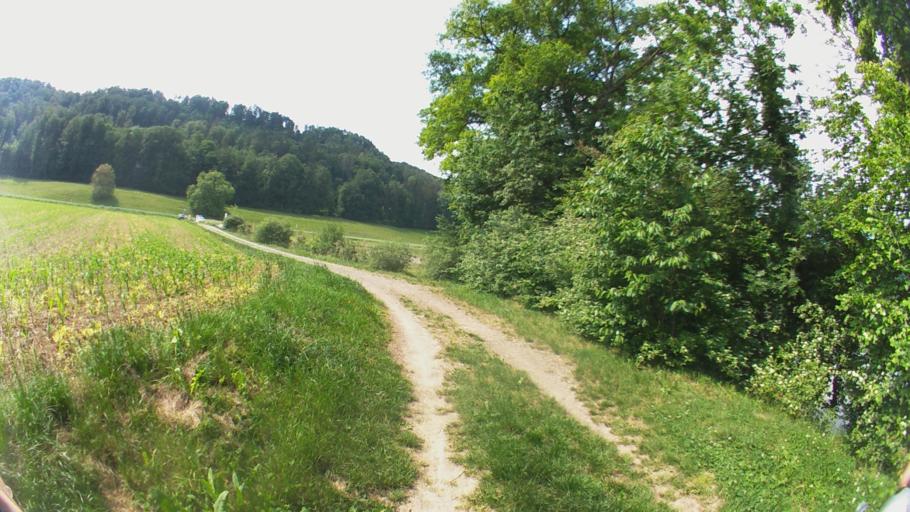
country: CH
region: Zurich
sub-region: Bezirk Buelach
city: Glattfelden
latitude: 47.5784
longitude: 8.4917
